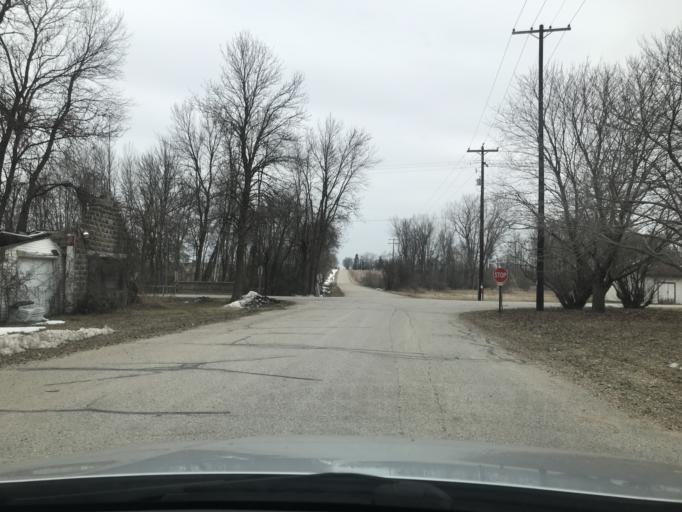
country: US
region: Wisconsin
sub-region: Marinette County
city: Peshtigo
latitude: 45.0483
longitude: -87.8511
